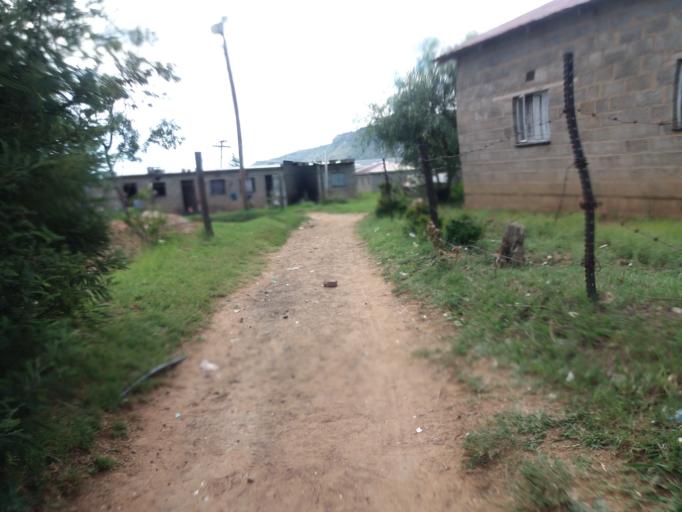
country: LS
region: Maseru
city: Maseru
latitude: -29.3667
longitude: 27.5055
